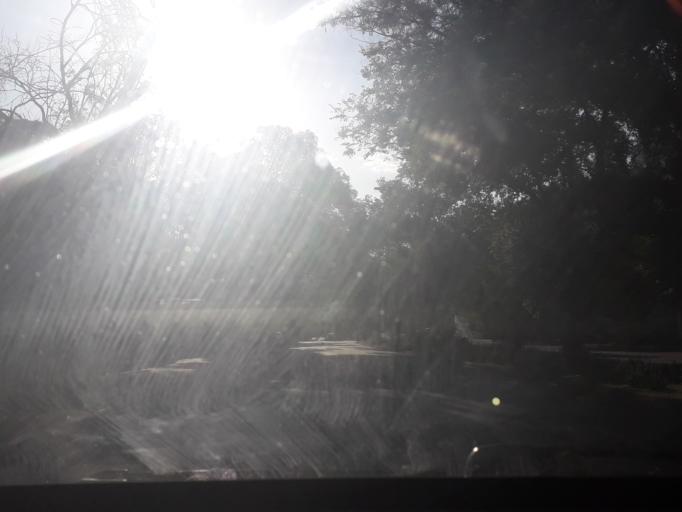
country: ZA
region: Gauteng
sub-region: City of Johannesburg Metropolitan Municipality
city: Johannesburg
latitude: -26.1493
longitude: 28.0408
